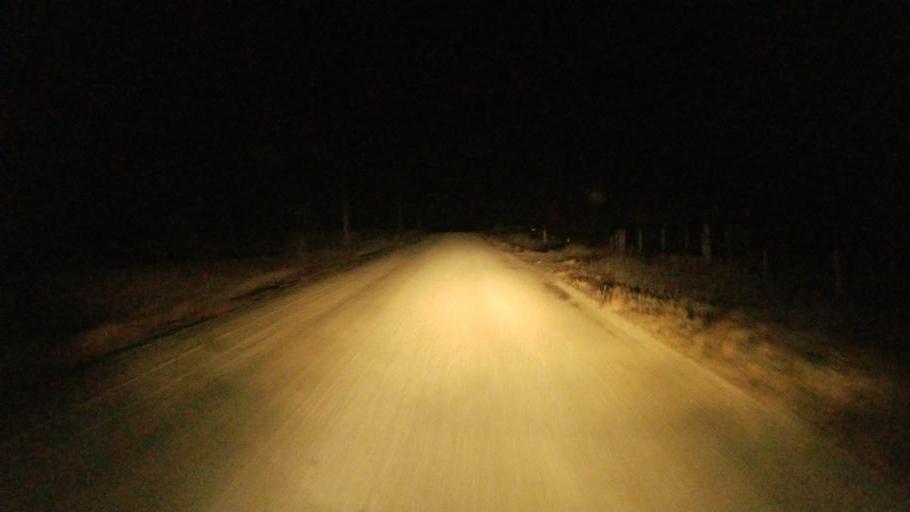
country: US
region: Nebraska
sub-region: Knox County
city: Center
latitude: 42.6260
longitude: -97.8274
